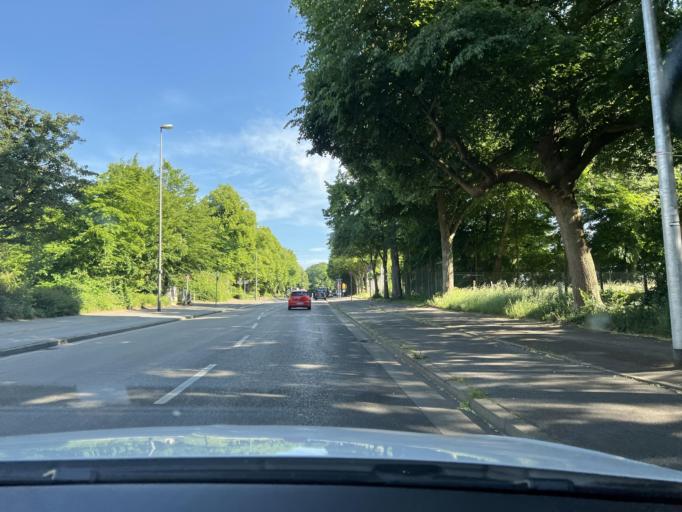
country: DE
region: North Rhine-Westphalia
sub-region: Regierungsbezirk Koln
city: Aachen
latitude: 50.7544
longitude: 6.0962
